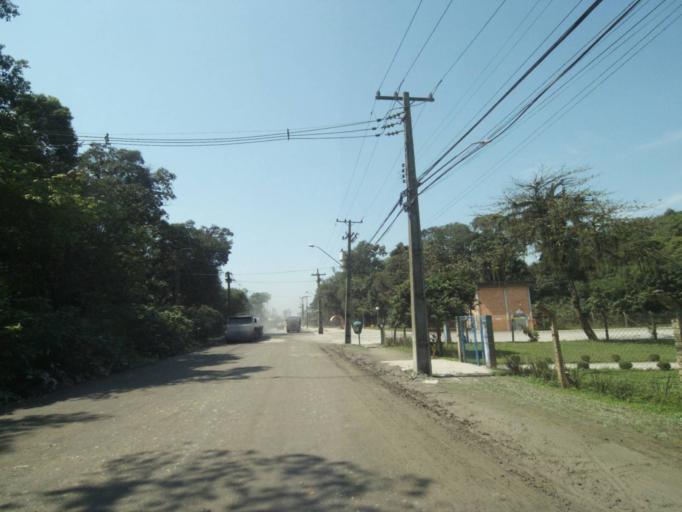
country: BR
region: Parana
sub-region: Paranagua
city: Paranagua
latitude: -25.5460
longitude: -48.5712
